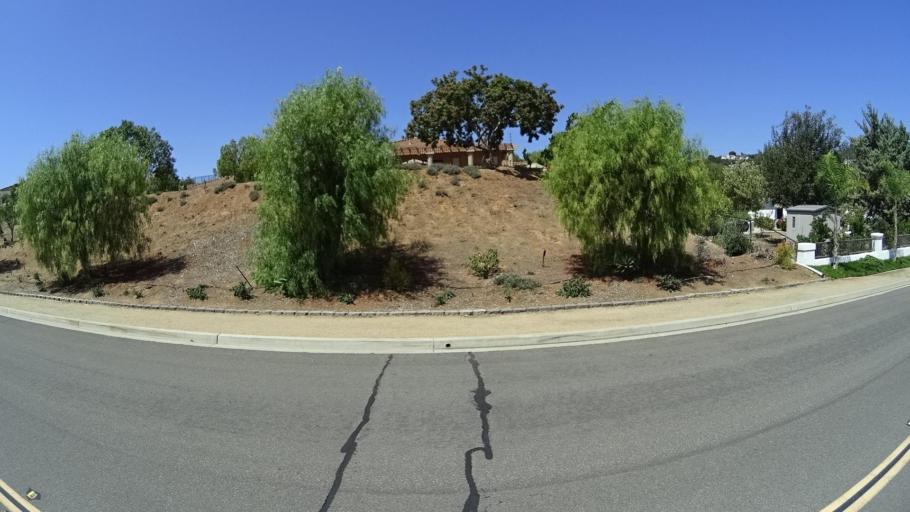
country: US
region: California
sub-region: San Diego County
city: Bonsall
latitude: 33.3270
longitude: -117.1970
